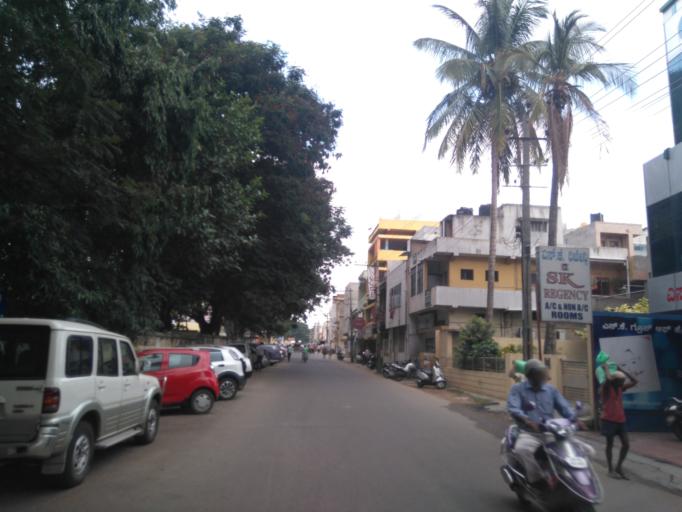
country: IN
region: Karnataka
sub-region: Mysore
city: Mysore
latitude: 12.3072
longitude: 76.6506
